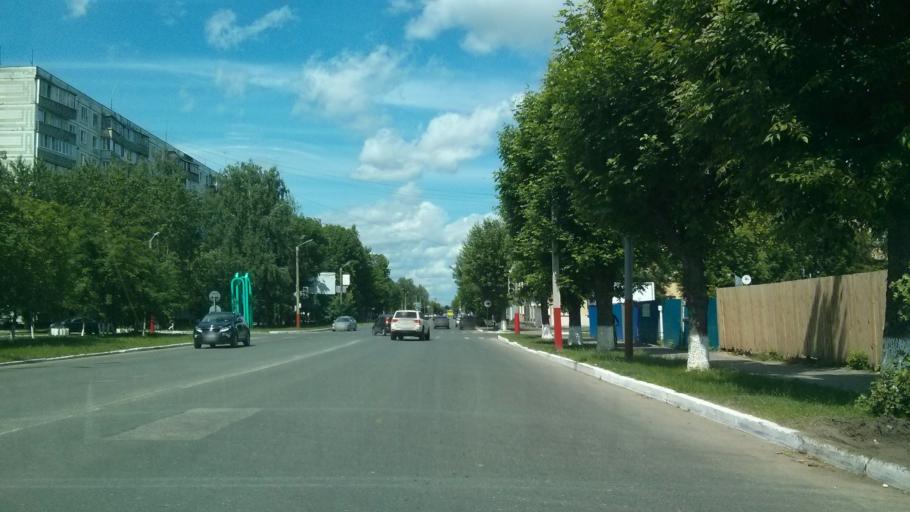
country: RU
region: Vladimir
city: Murom
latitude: 55.5699
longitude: 42.0592
